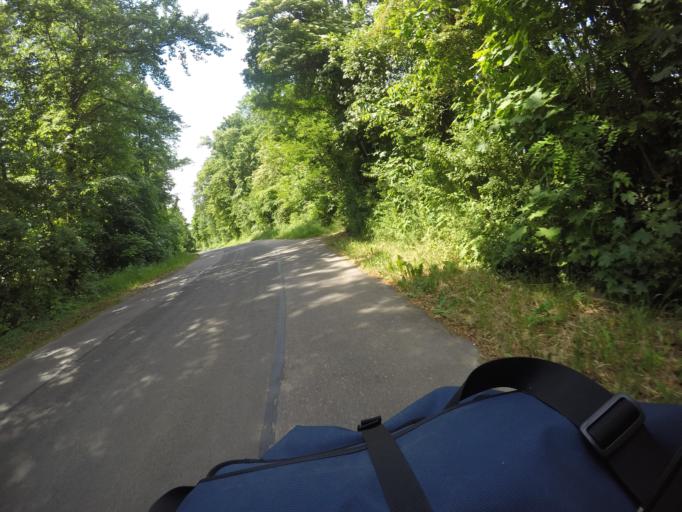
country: DE
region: Baden-Wuerttemberg
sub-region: Karlsruhe Region
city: Weingarten
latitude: 48.9924
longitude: 8.4965
